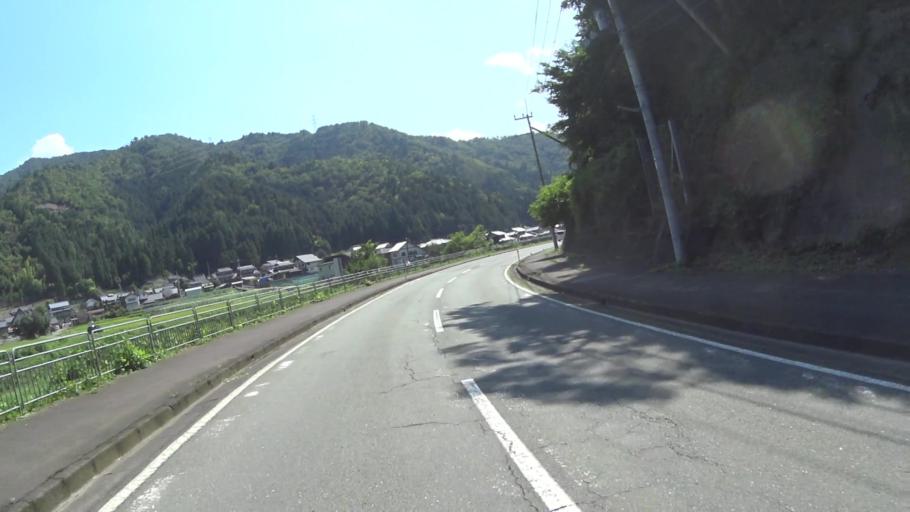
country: JP
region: Fukui
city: Obama
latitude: 35.4033
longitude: 135.6890
